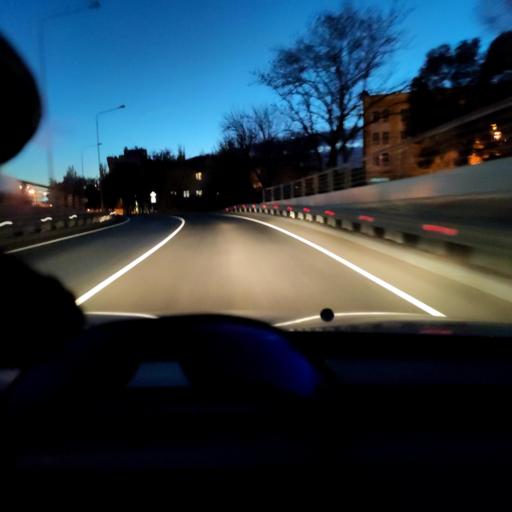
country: RU
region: Samara
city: Rozhdestveno
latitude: 53.1782
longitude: 50.0817
